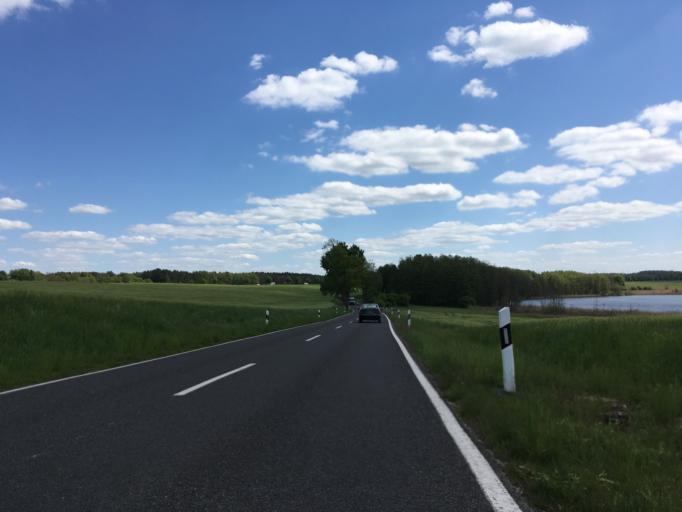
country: DE
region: Brandenburg
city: Biesenthal
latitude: 52.7604
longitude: 13.6377
